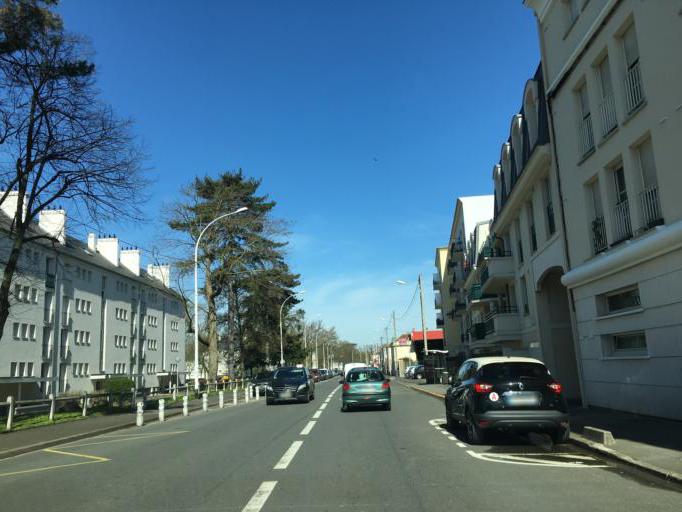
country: FR
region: Ile-de-France
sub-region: Departement de l'Essonne
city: Draveil
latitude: 48.6804
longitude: 2.4095
